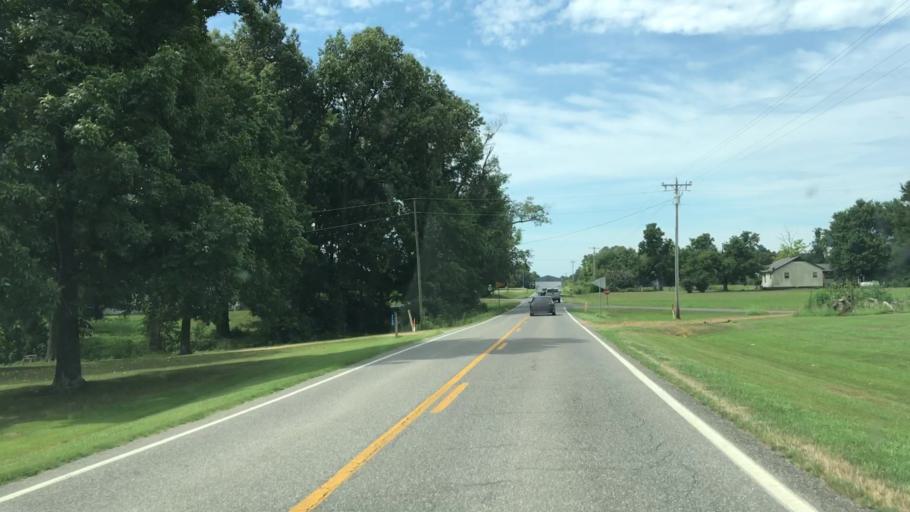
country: US
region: Kentucky
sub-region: Graves County
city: Mayfield
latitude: 36.8476
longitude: -88.5754
